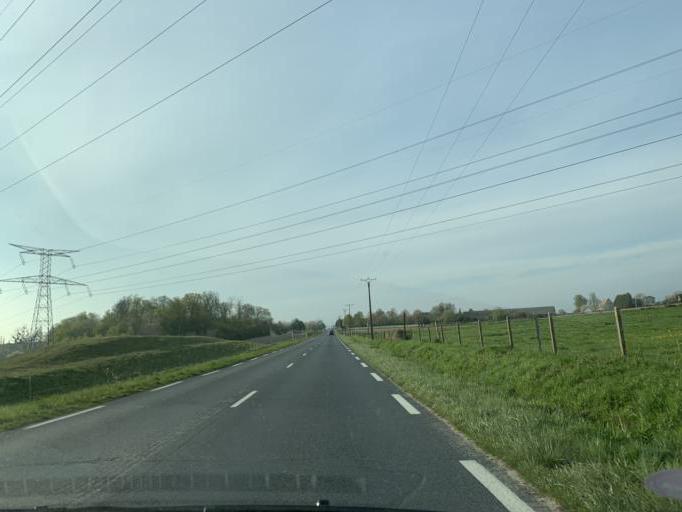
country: FR
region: Haute-Normandie
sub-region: Departement de l'Eure
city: Bourg-Achard
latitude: 49.3787
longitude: 0.8046
